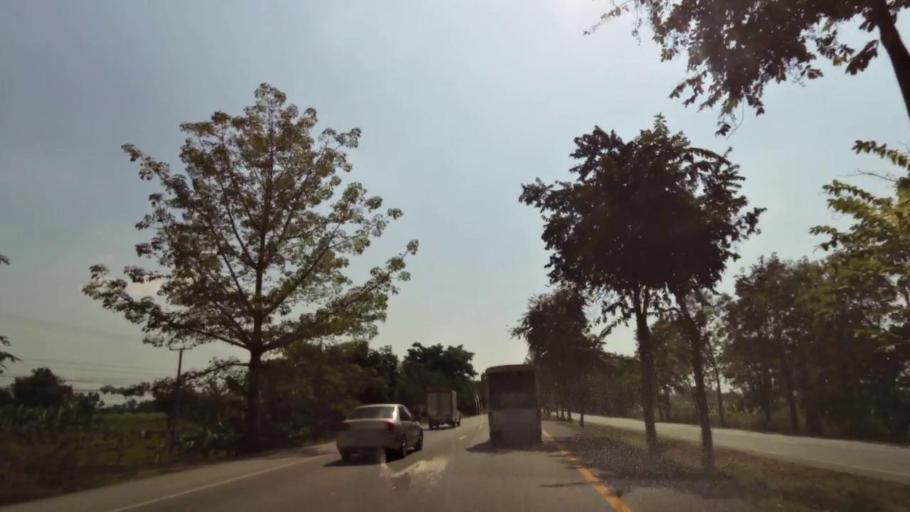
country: TH
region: Phichit
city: Bueng Na Rang
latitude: 16.1089
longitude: 100.1258
